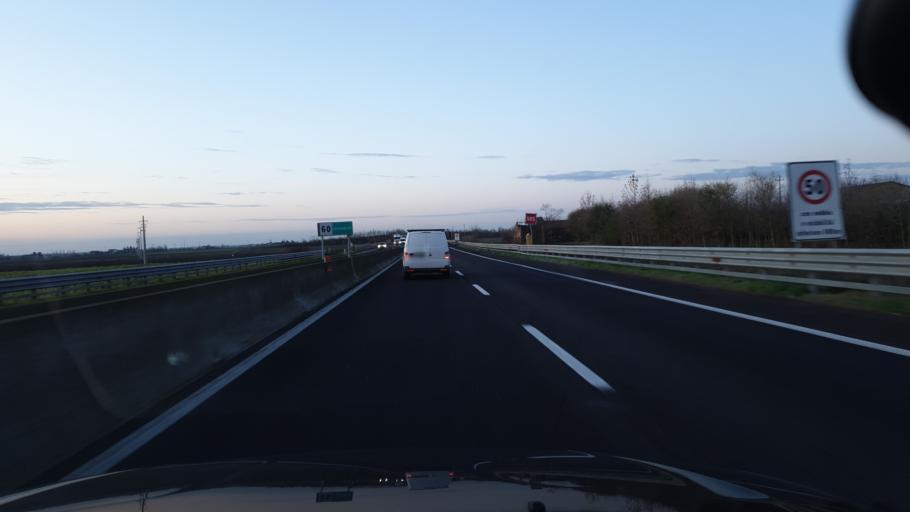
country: IT
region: Veneto
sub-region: Provincia di Rovigo
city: Villamarzana
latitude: 45.0020
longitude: 11.6761
